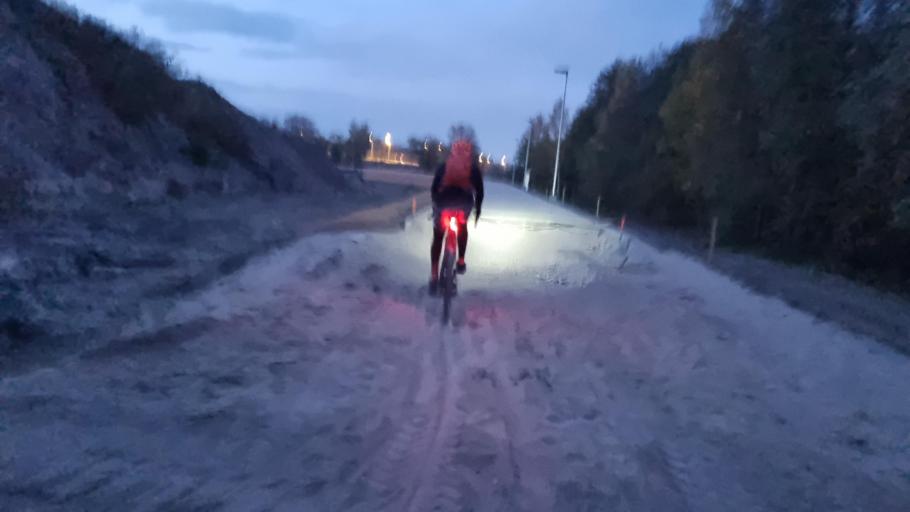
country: LV
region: Riga
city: Daugavgriva
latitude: 57.0347
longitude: 24.0374
